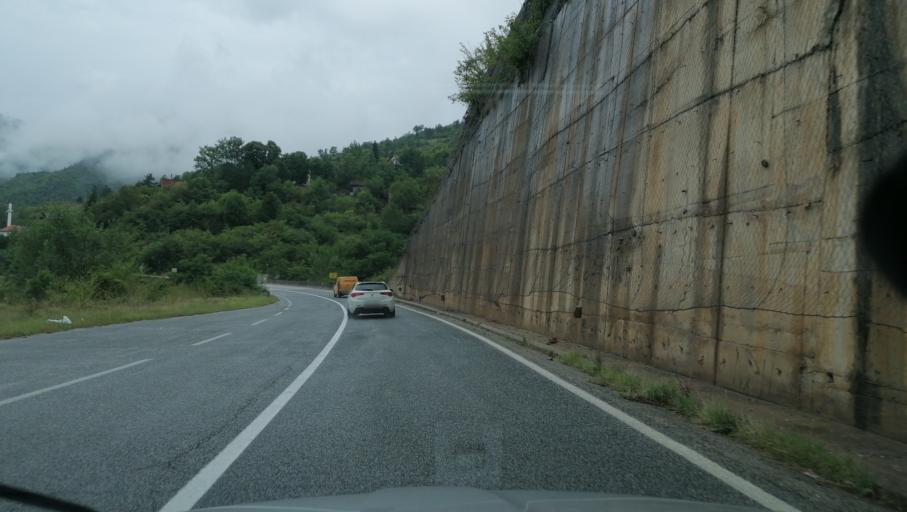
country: BA
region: Republika Srpska
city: Visegrad
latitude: 43.7331
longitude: 19.1843
